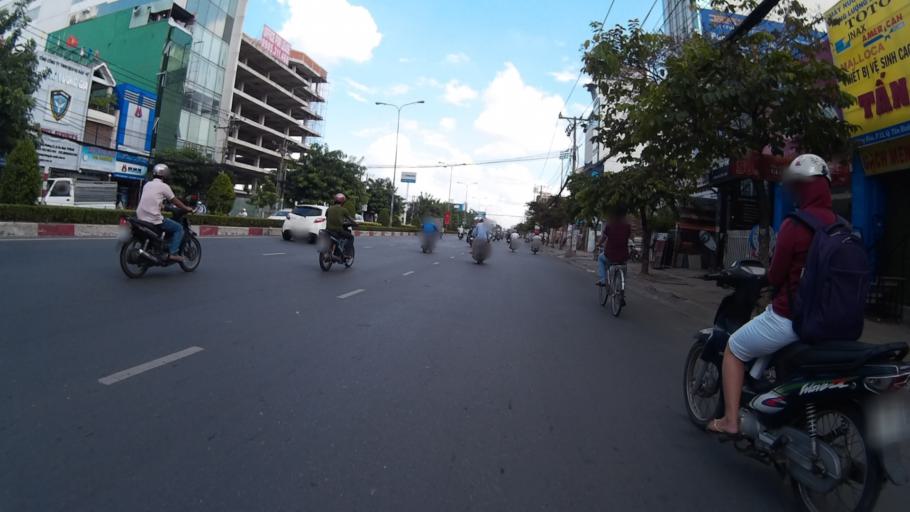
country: VN
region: Ho Chi Minh City
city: Quan Tan Phu
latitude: 10.8014
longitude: 106.6514
